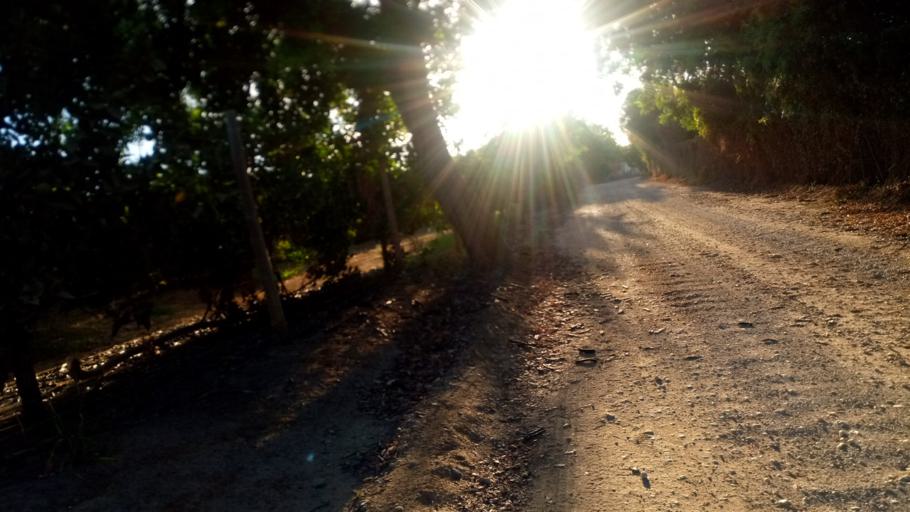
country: PT
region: Faro
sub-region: Tavira
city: Tavira
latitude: 37.1476
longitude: -7.5875
